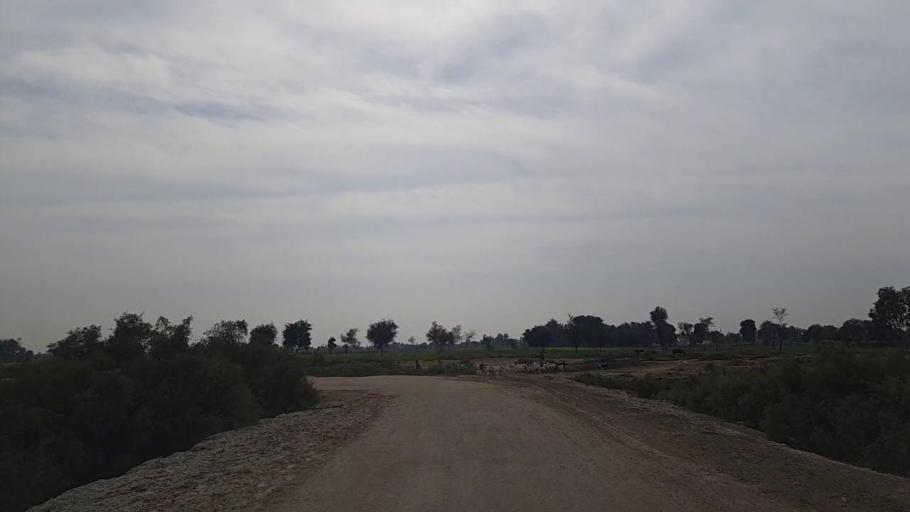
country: PK
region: Sindh
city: Daur
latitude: 26.4298
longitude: 68.4713
